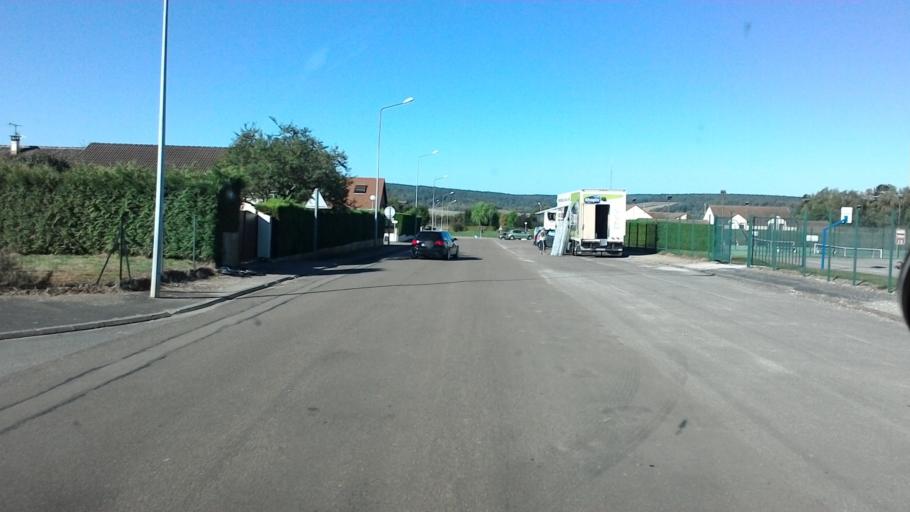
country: FR
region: Champagne-Ardenne
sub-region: Departement de la Haute-Marne
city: Chateauvillain
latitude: 48.0275
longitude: 4.9144
